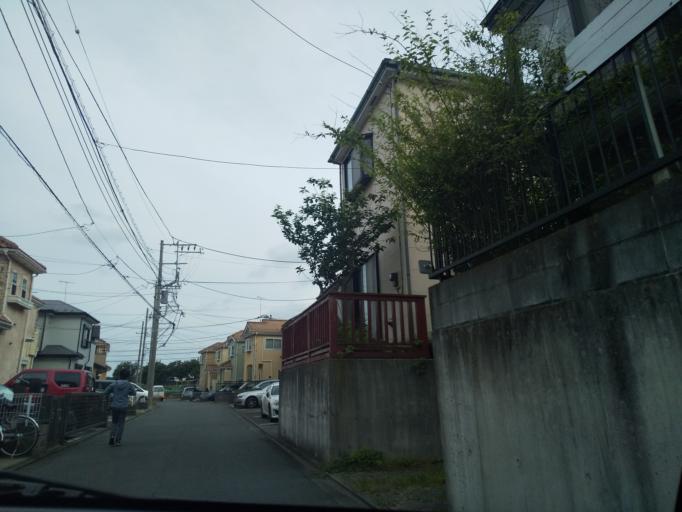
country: JP
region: Kanagawa
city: Zama
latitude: 35.5451
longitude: 139.3697
